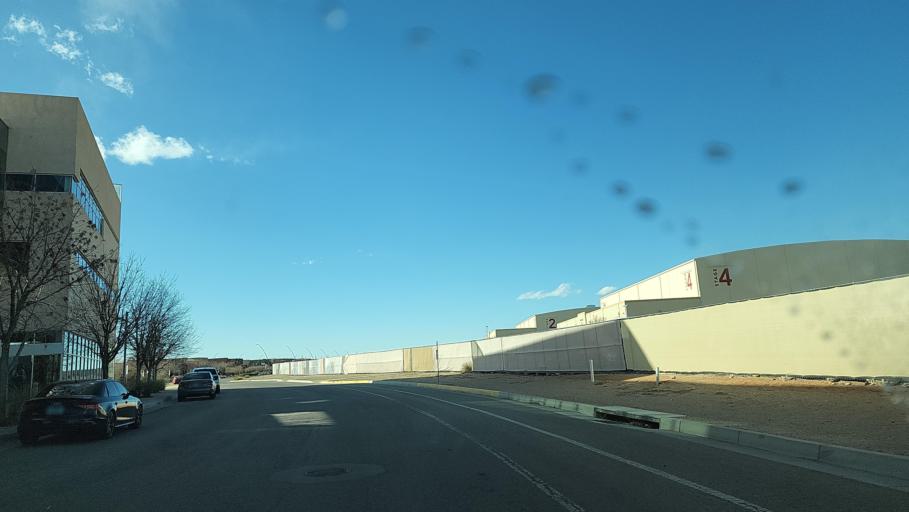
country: US
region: New Mexico
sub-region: Bernalillo County
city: South Valley
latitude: 34.9870
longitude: -106.6126
